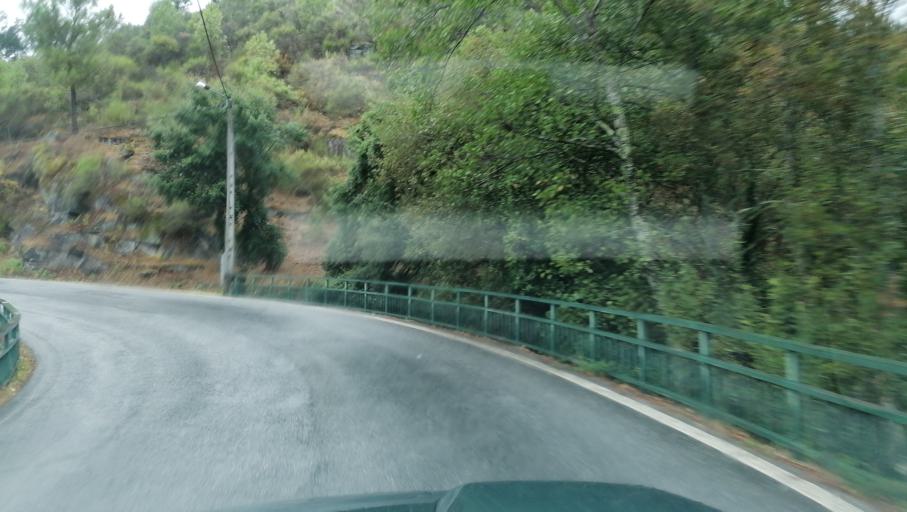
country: PT
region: Braga
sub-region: Cabeceiras de Basto
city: Cabeceiras de Basto
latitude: 41.4946
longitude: -7.9420
